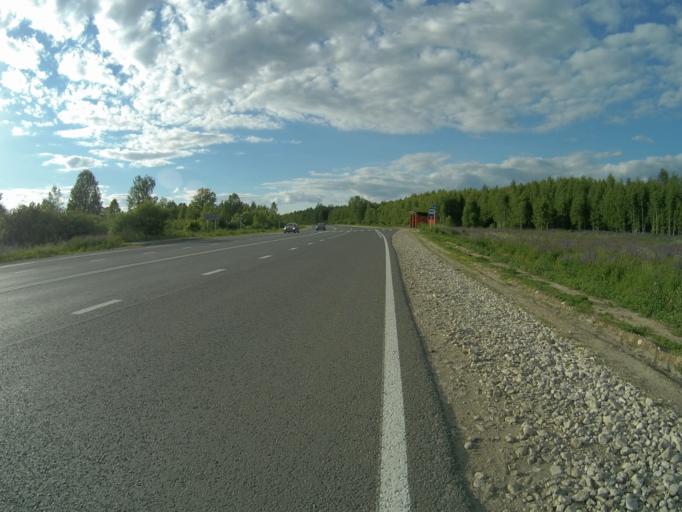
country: RU
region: Vladimir
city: Anopino
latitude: 55.7934
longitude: 40.6829
